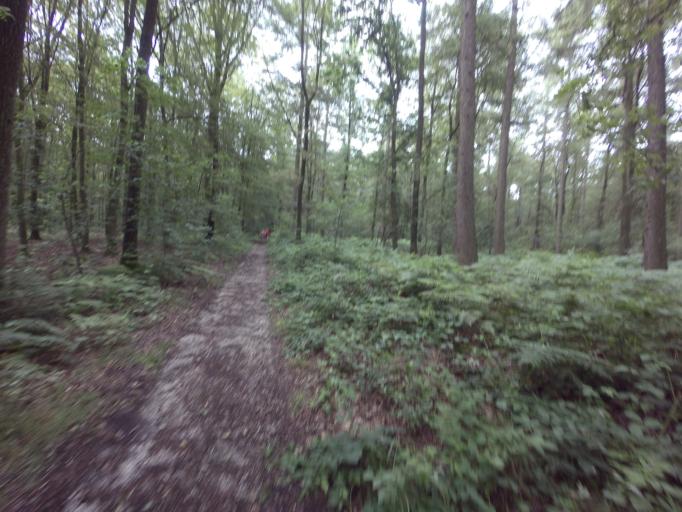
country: BE
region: Wallonia
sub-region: Province de Liege
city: Plombieres
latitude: 50.7636
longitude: 5.9743
